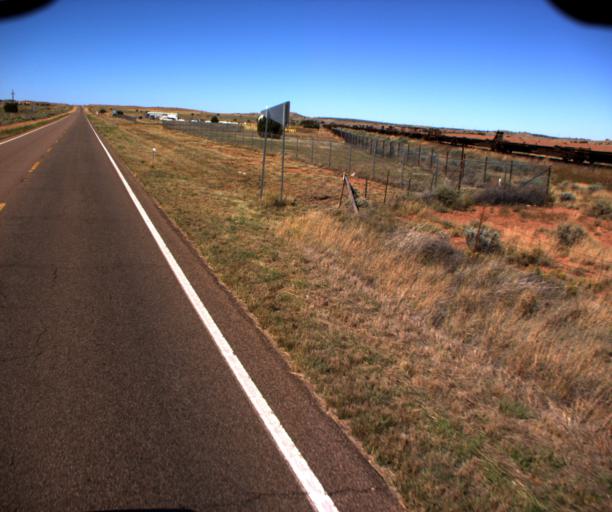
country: US
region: Arizona
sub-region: Navajo County
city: Snowflake
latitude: 34.5130
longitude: -110.1321
